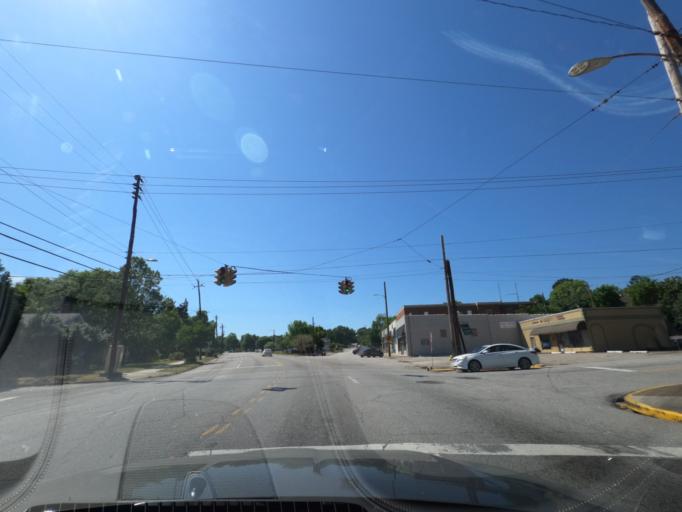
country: US
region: Georgia
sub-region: Richmond County
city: Augusta
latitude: 33.4702
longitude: -82.0120
